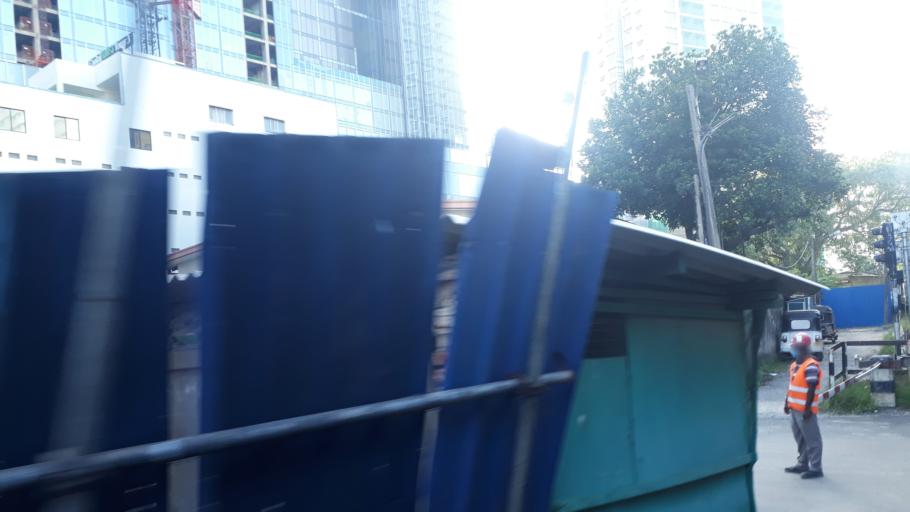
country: LK
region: Western
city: Colombo
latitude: 6.9249
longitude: 79.8491
